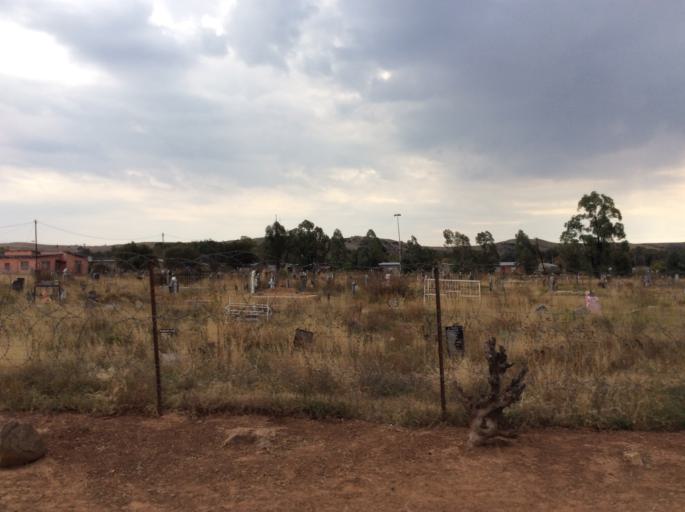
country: ZA
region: Orange Free State
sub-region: Xhariep District Municipality
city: Dewetsdorp
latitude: -29.5830
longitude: 26.6743
